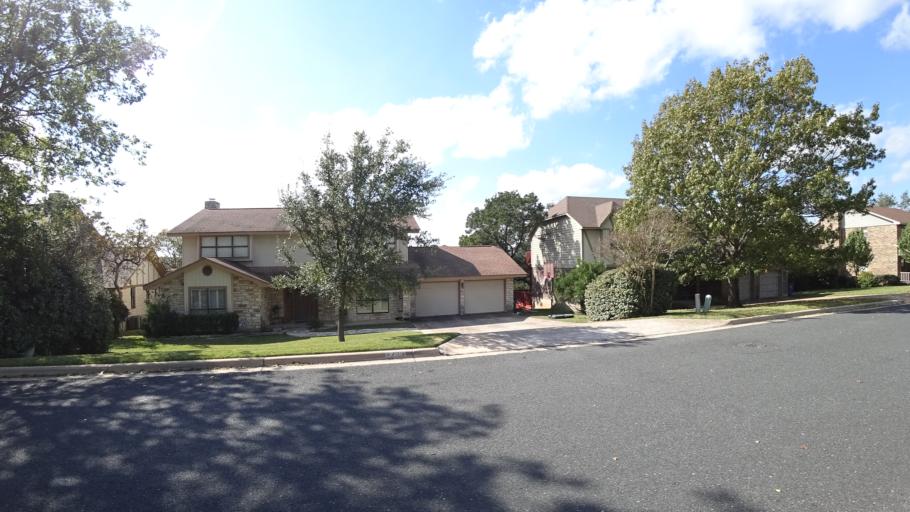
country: US
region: Texas
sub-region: Williamson County
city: Anderson Mill
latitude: 30.4218
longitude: -97.8053
